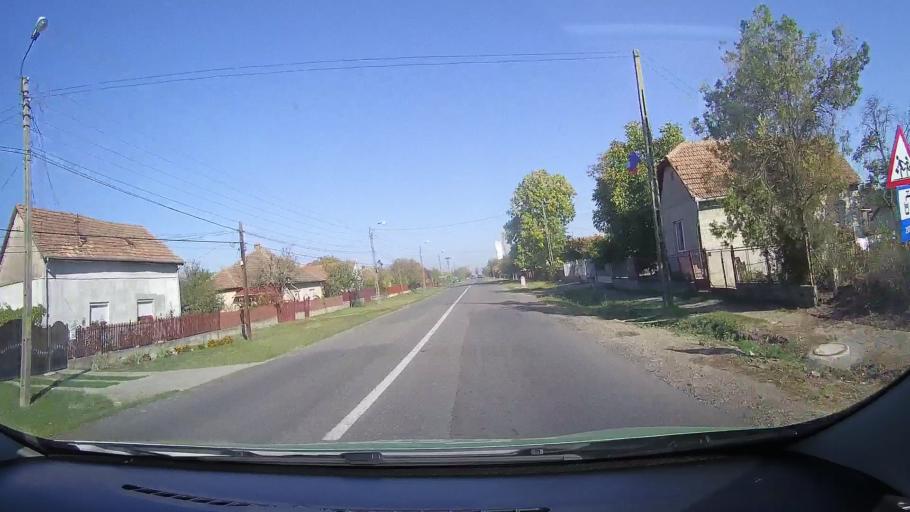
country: RO
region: Satu Mare
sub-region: Oras Tasnad
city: Tasnad
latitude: 47.5099
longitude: 22.5731
